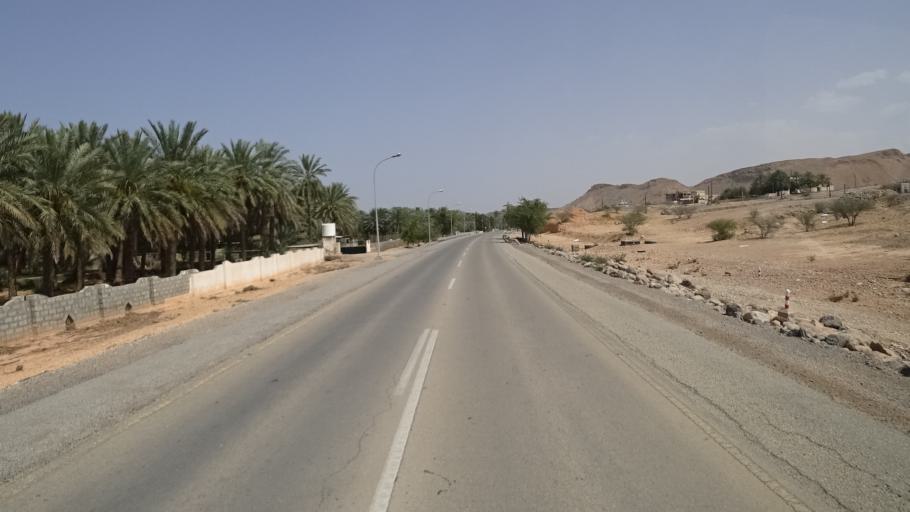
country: OM
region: Muhafazat Masqat
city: Muscat
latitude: 23.1744
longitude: 58.9105
